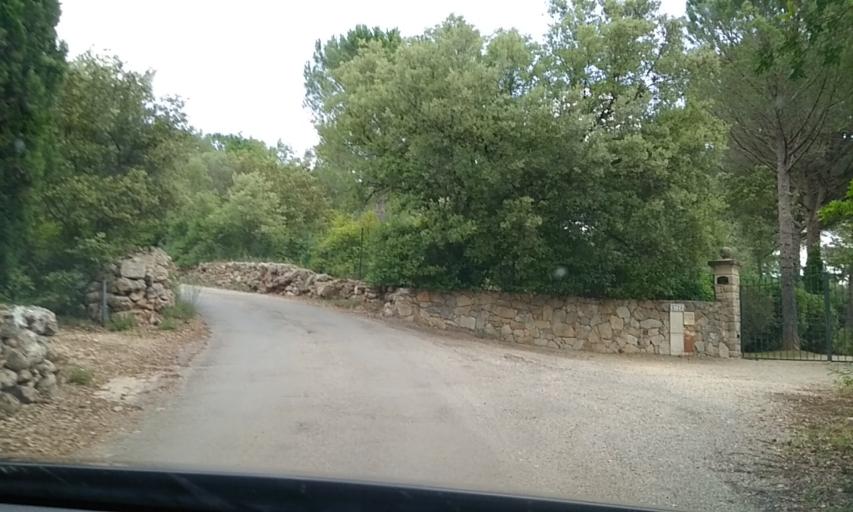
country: FR
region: Provence-Alpes-Cote d'Azur
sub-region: Departement du Var
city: Cotignac
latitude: 43.5144
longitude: 6.1532
